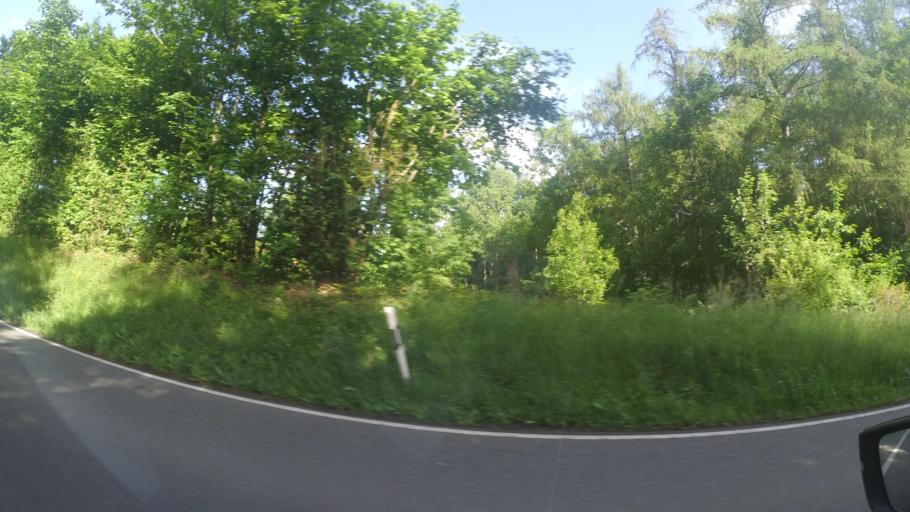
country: DE
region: Rheinland-Pfalz
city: Wernersberg
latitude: 49.1763
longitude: 7.9430
